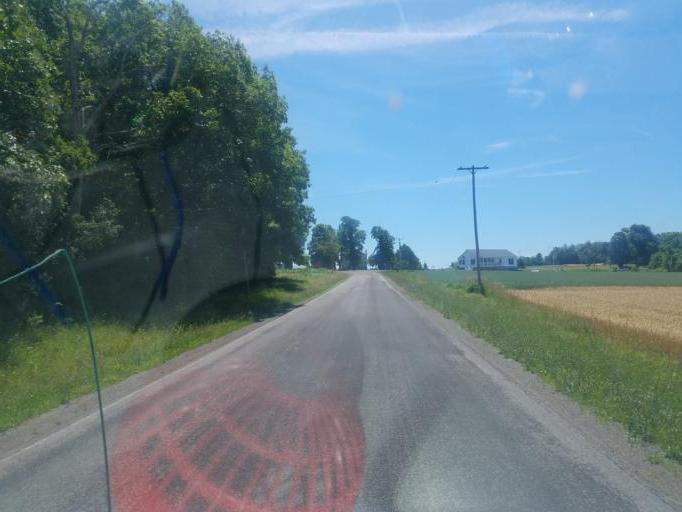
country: US
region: New York
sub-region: Yates County
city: Penn Yan
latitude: 42.6342
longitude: -77.0158
